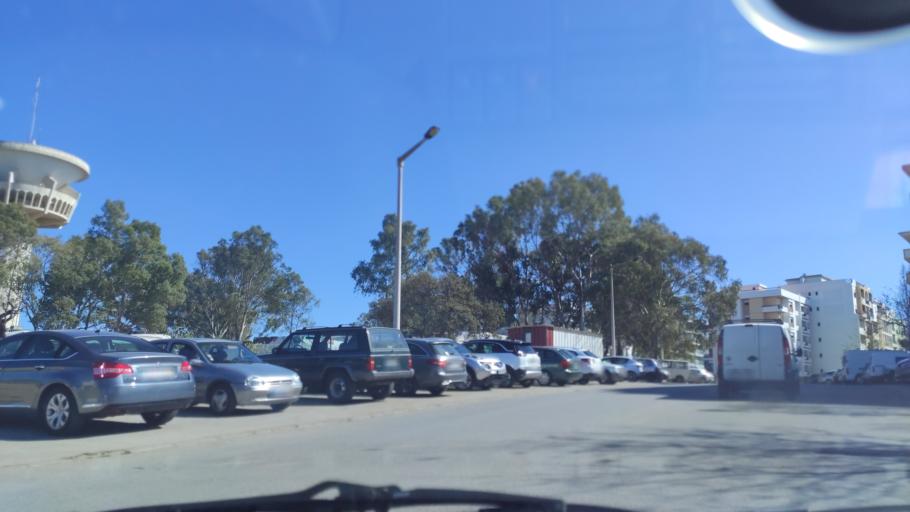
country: PT
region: Faro
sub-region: Faro
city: Faro
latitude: 37.0280
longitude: -7.9360
